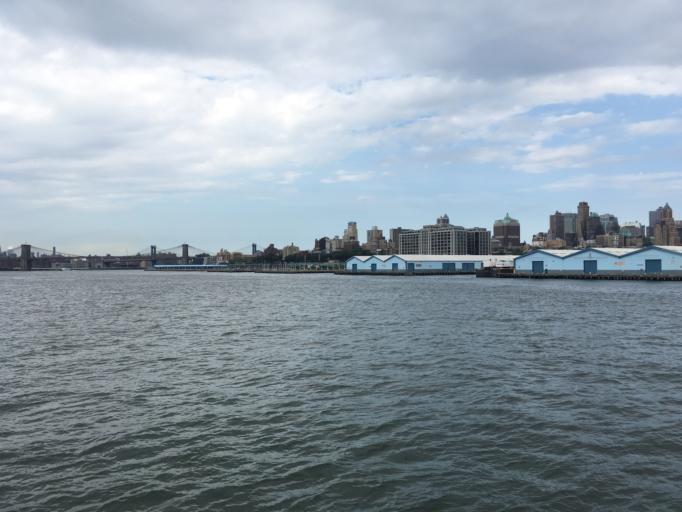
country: US
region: New York
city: New York City
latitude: 40.6901
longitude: -74.0085
